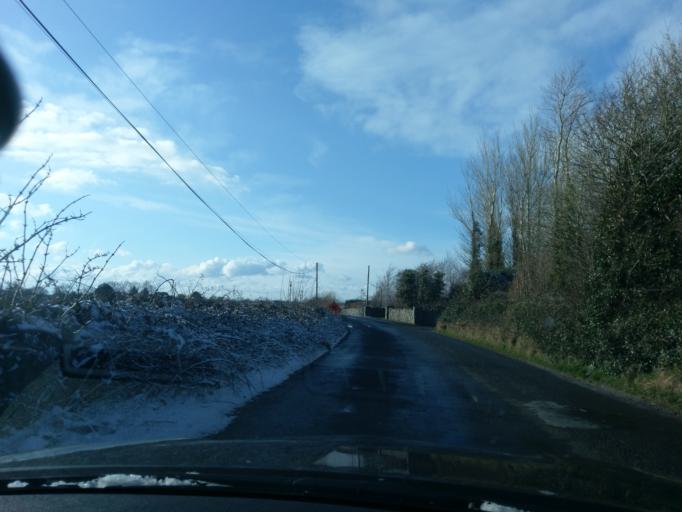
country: IE
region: Connaught
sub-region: County Galway
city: Oranmore
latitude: 53.2000
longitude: -8.8445
